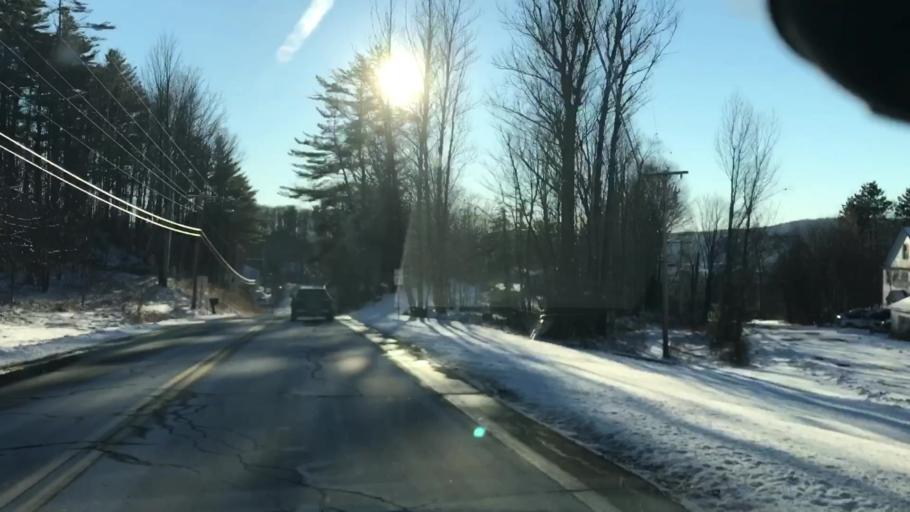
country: US
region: New Hampshire
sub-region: Grafton County
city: Haverhill
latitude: 44.0452
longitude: -72.0558
